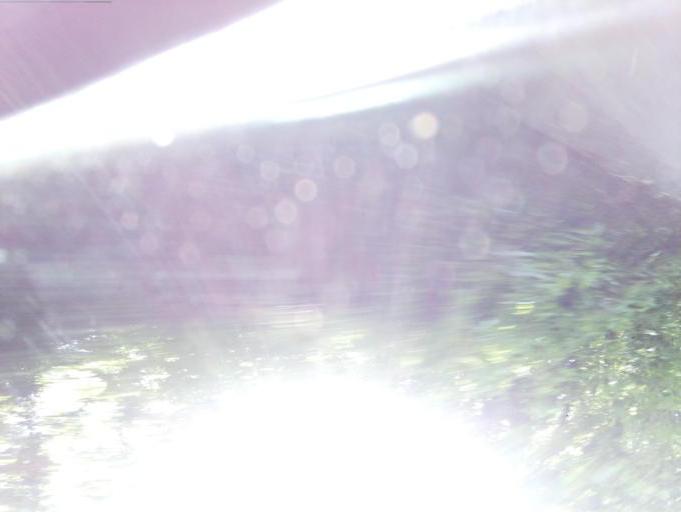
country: GB
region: England
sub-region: Somerset
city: Yeovil
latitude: 50.9401
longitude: -2.6017
